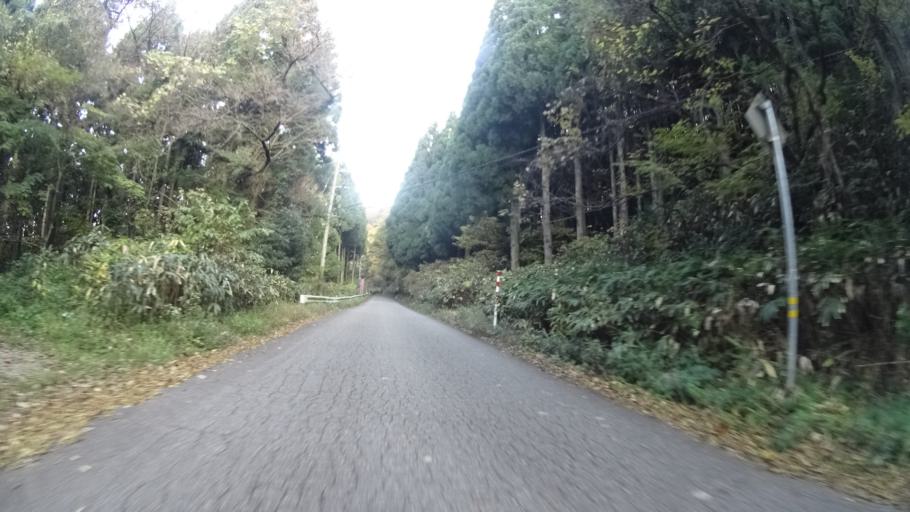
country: JP
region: Ishikawa
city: Nanao
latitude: 37.0118
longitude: 136.9887
